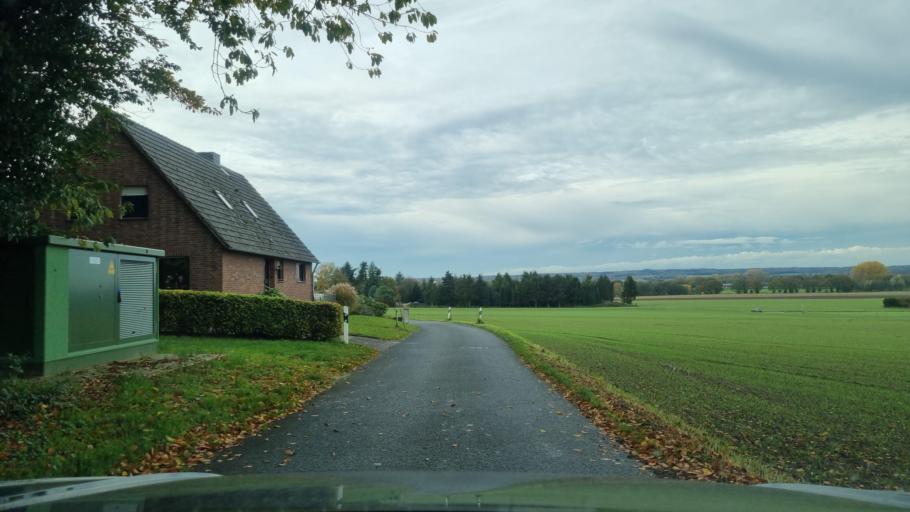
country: DE
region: North Rhine-Westphalia
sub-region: Regierungsbezirk Dusseldorf
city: Kranenburg
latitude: 51.7742
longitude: 6.0094
